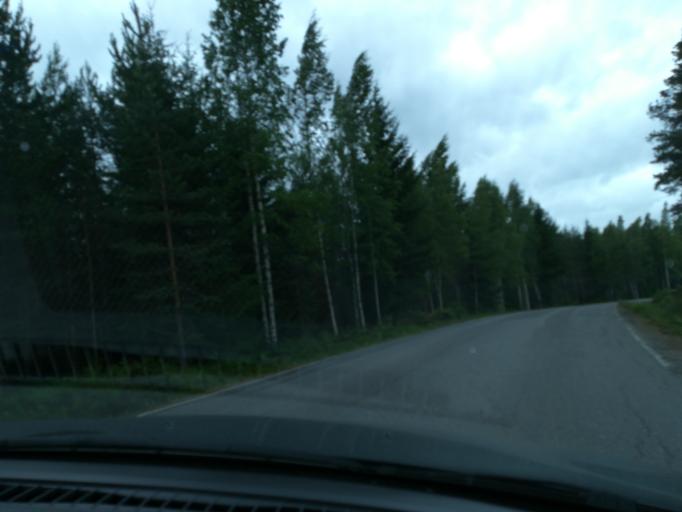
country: FI
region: South Karelia
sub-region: Lappeenranta
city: Savitaipale
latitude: 61.3237
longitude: 27.4784
